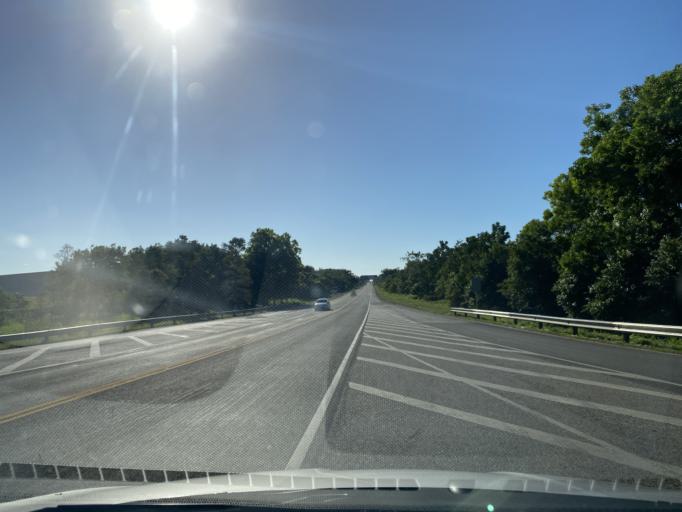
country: DO
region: Santo Domingo
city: Guerra
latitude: 18.5251
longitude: -69.7487
